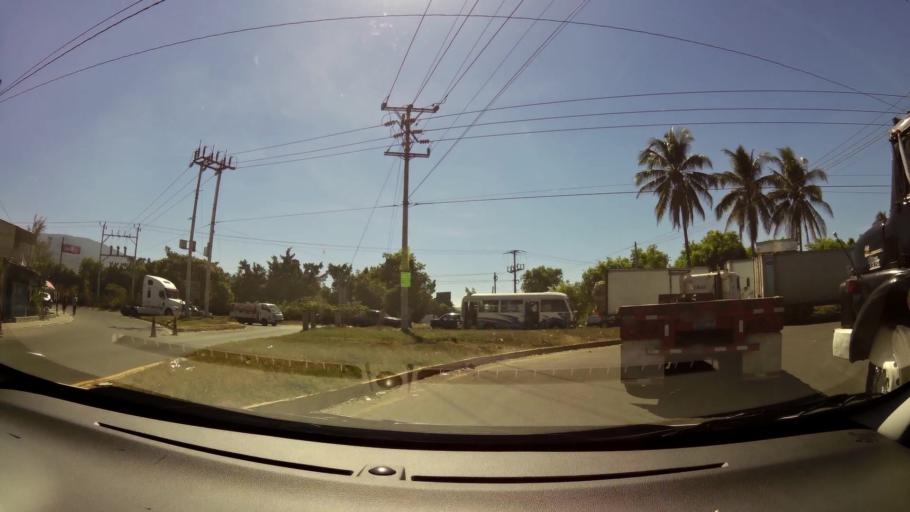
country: SV
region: La Libertad
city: Ciudad Arce
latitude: 13.7804
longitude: -89.3723
